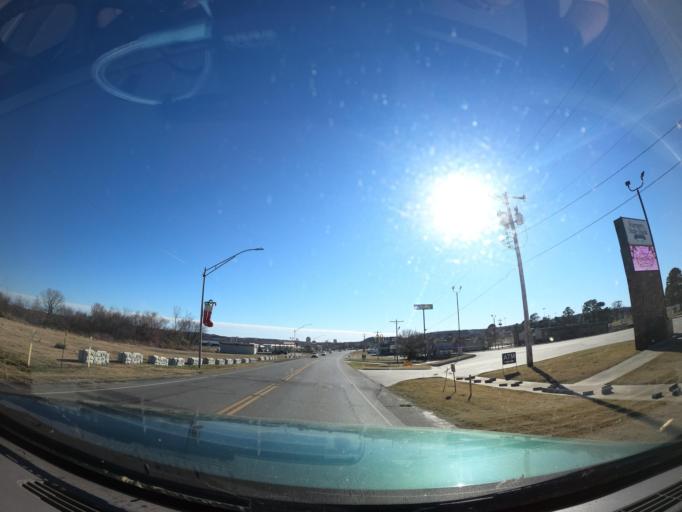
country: US
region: Oklahoma
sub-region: McIntosh County
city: Eufaula
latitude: 35.2817
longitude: -95.5828
